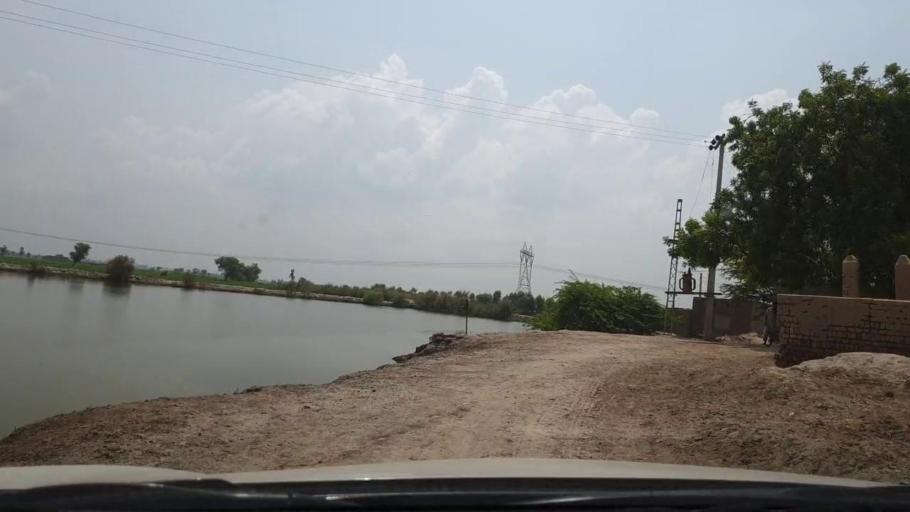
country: PK
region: Sindh
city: New Badah
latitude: 27.3878
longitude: 68.0419
